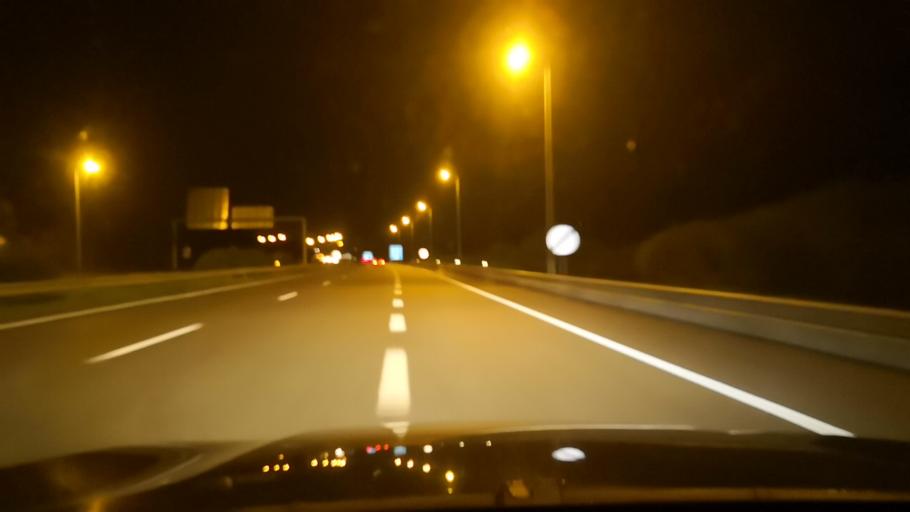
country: PT
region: Setubal
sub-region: Palmela
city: Palmela
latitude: 38.5592
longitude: -8.8684
